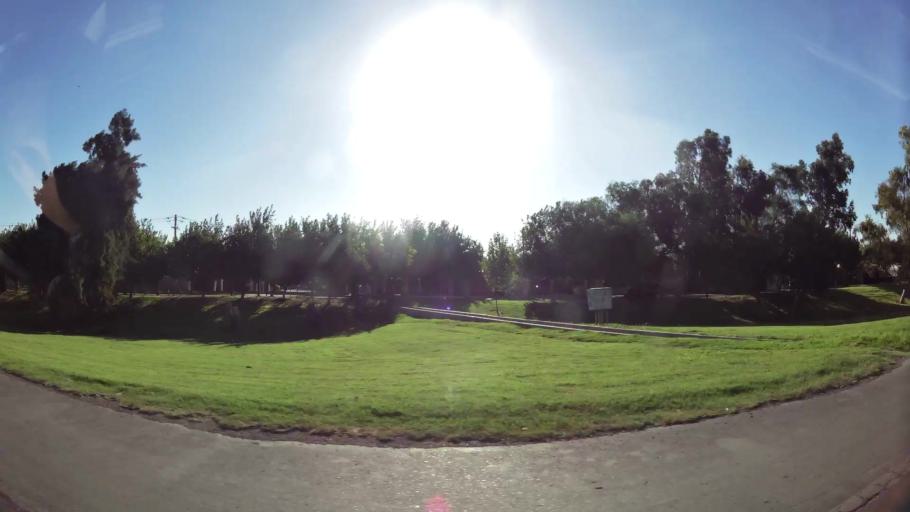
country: AR
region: San Juan
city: Villa Krause
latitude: -31.5639
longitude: -68.5158
